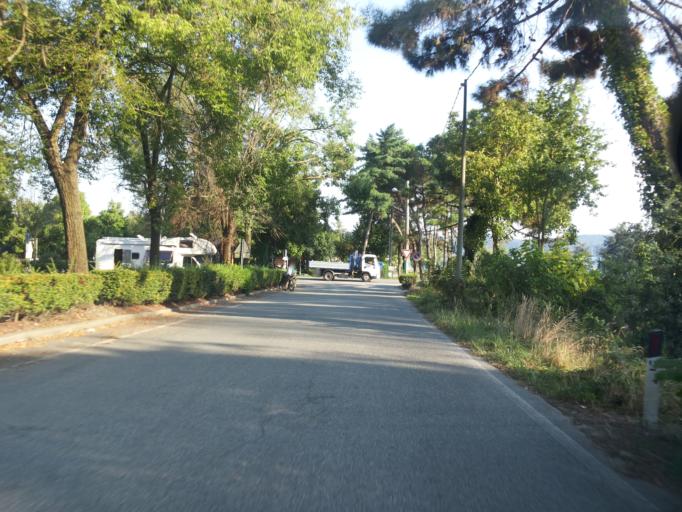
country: IT
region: Piedmont
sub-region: Provincia di Biella
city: Zimone
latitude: 45.4323
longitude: 8.0315
